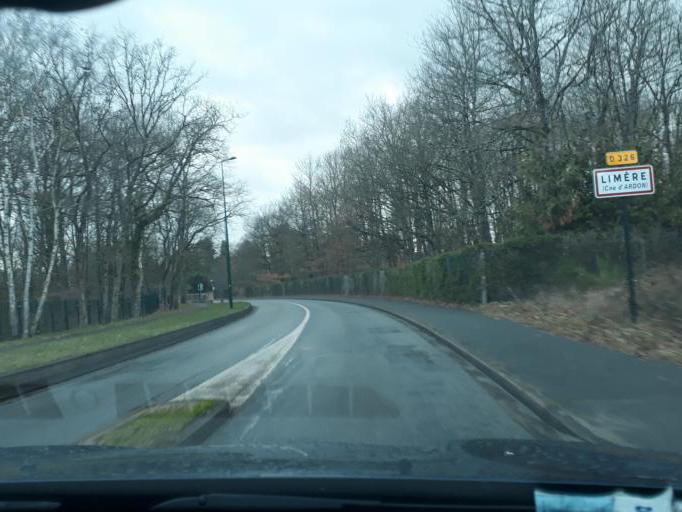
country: FR
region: Centre
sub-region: Departement du Loiret
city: Olivet
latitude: 47.8296
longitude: 1.9159
